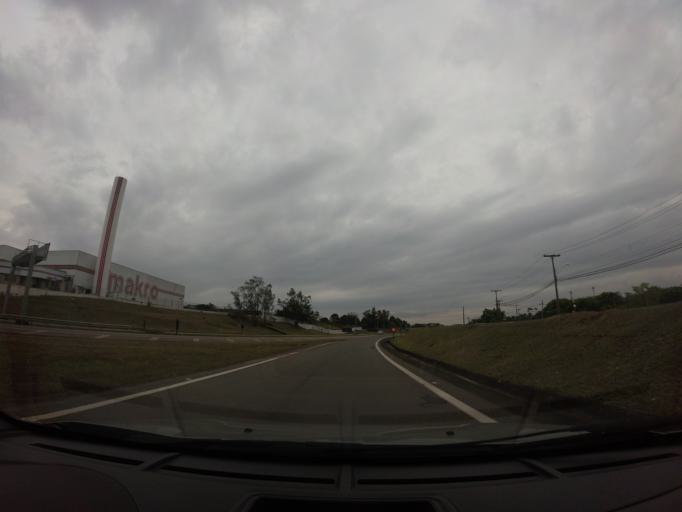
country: BR
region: Sao Paulo
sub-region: Piracicaba
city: Piracicaba
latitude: -22.7410
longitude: -47.6003
